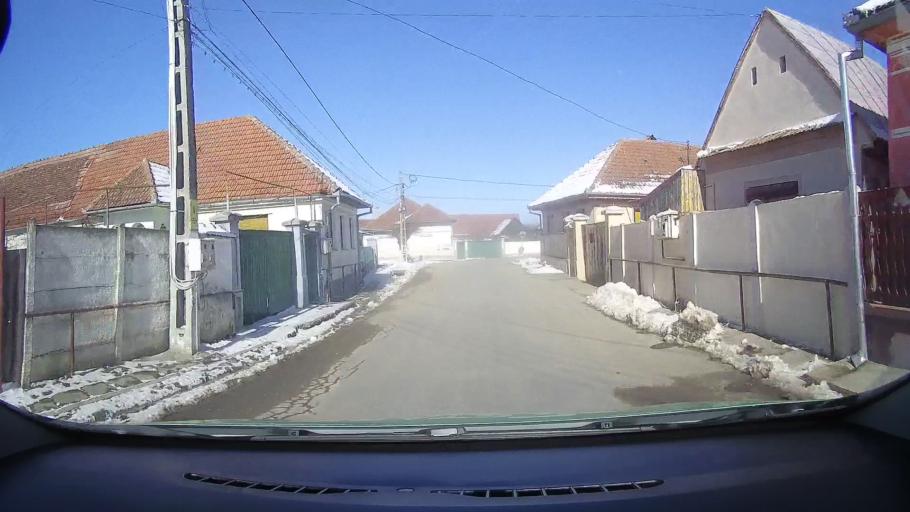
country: RO
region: Brasov
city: Ucea de Sus
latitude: 45.7505
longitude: 24.6790
